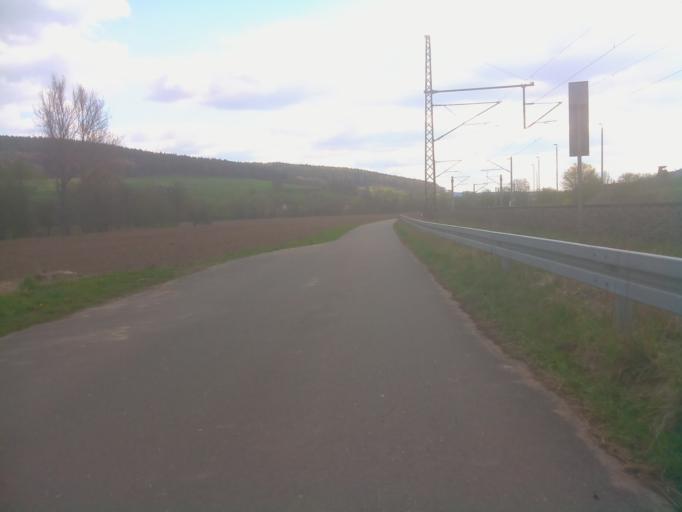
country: DE
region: Thuringia
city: Schops
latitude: 50.8301
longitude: 11.5971
